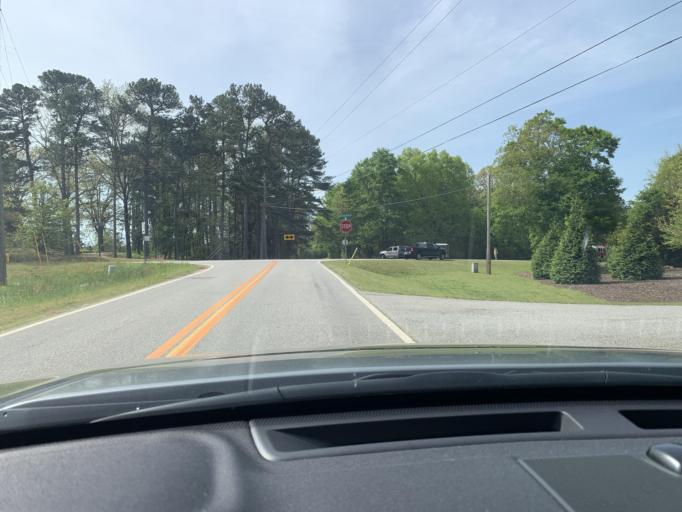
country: US
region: Georgia
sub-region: Oconee County
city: Watkinsville
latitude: 33.8328
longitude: -83.4876
